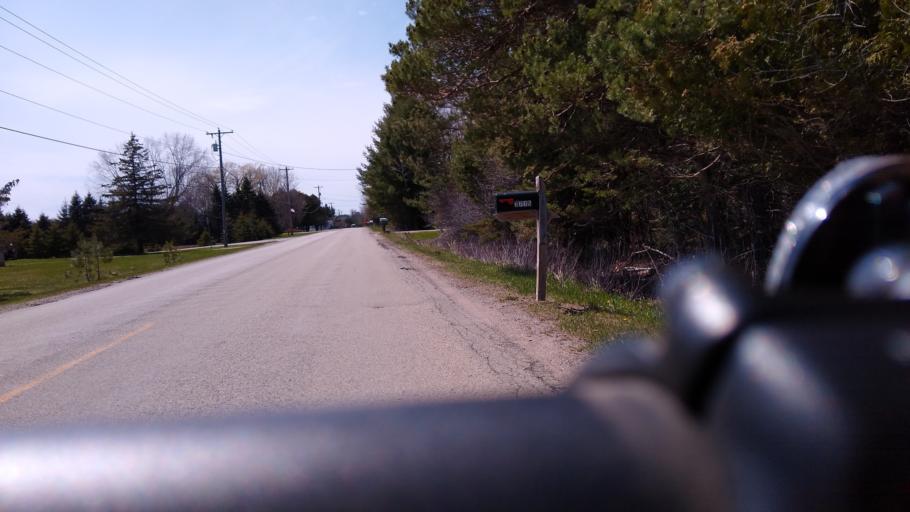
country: US
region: Michigan
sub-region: Delta County
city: Escanaba
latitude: 45.7353
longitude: -87.1819
